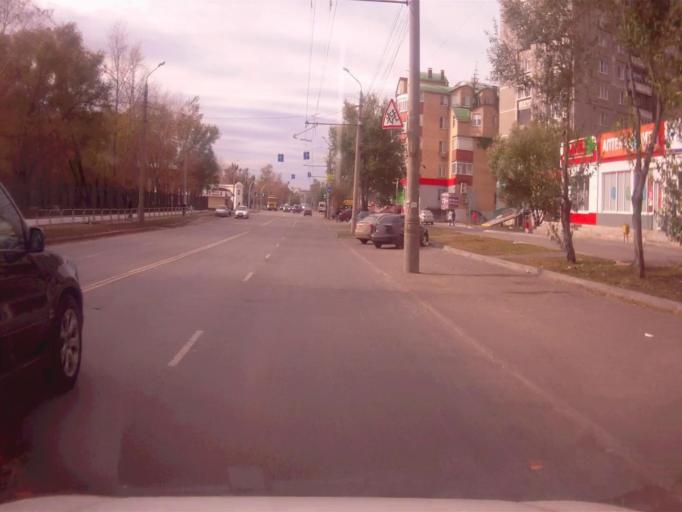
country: RU
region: Chelyabinsk
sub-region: Gorod Chelyabinsk
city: Chelyabinsk
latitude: 55.1131
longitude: 61.4602
